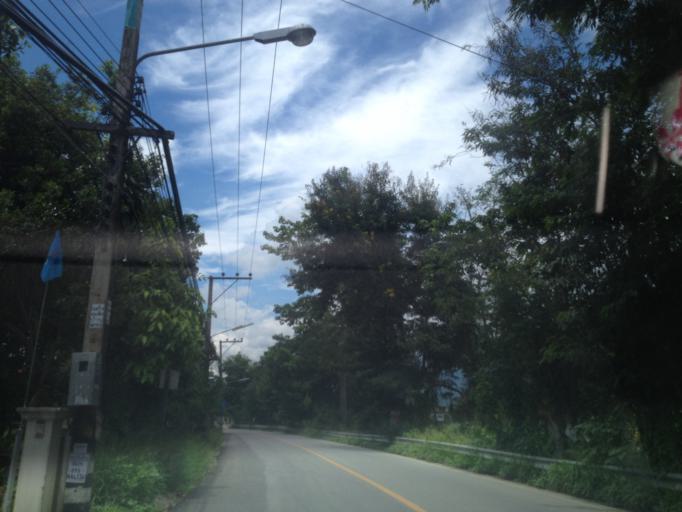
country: TH
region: Chiang Mai
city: Chiang Mai
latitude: 18.7369
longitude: 98.9830
